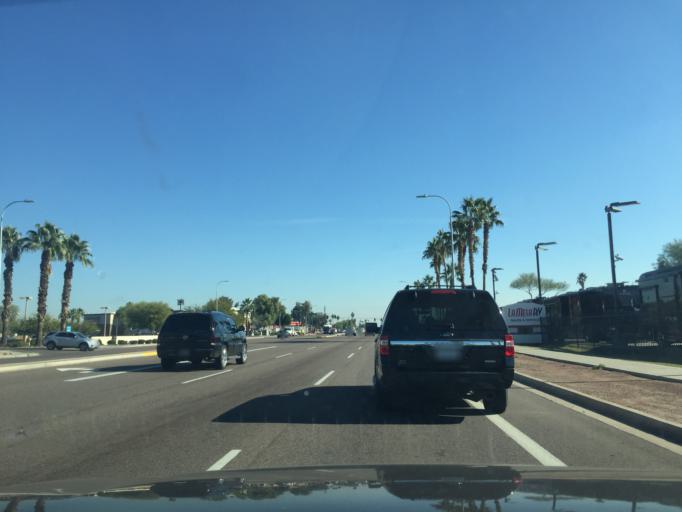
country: US
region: Arizona
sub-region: Maricopa County
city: Tolleson
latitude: 33.4655
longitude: -112.2232
